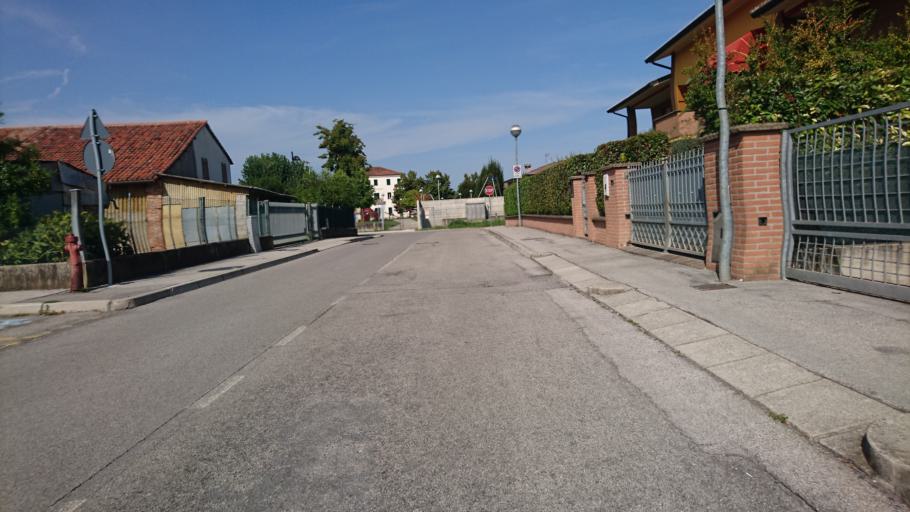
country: IT
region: Veneto
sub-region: Provincia di Padova
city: Veggiano
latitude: 45.4467
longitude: 11.7132
